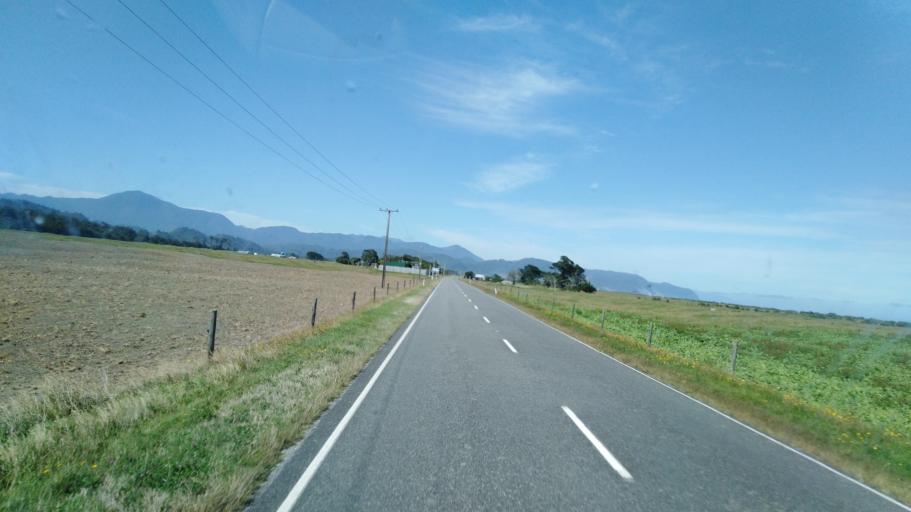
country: NZ
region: West Coast
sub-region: Buller District
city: Westport
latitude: -41.3173
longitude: 172.0894
